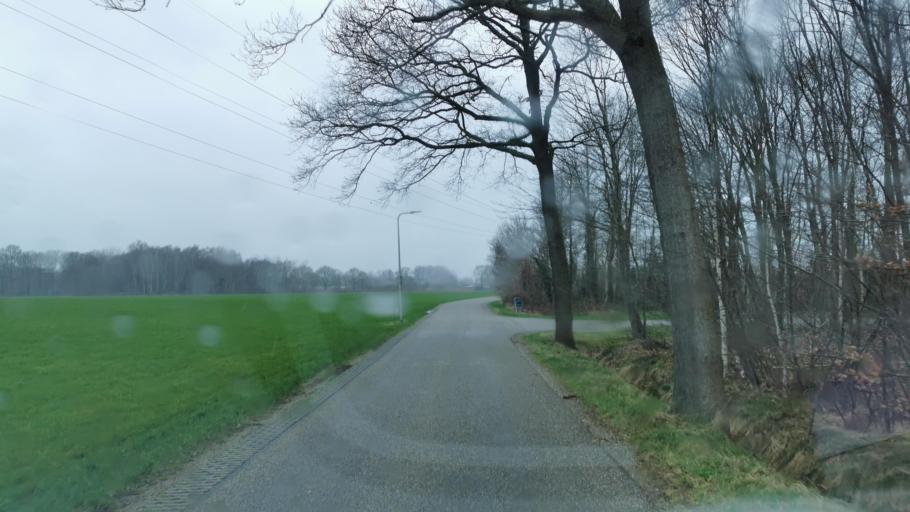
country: NL
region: Overijssel
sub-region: Gemeente Oldenzaal
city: Oldenzaal
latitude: 52.2972
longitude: 6.8706
